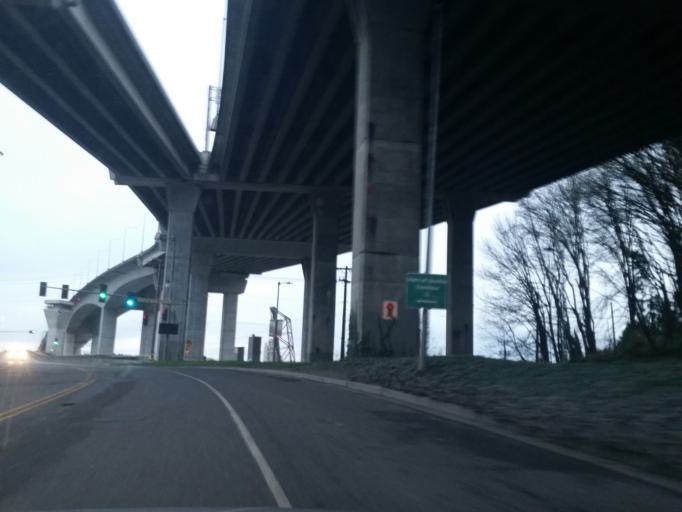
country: US
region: Washington
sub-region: King County
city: Seattle
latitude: 47.5714
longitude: -122.3584
